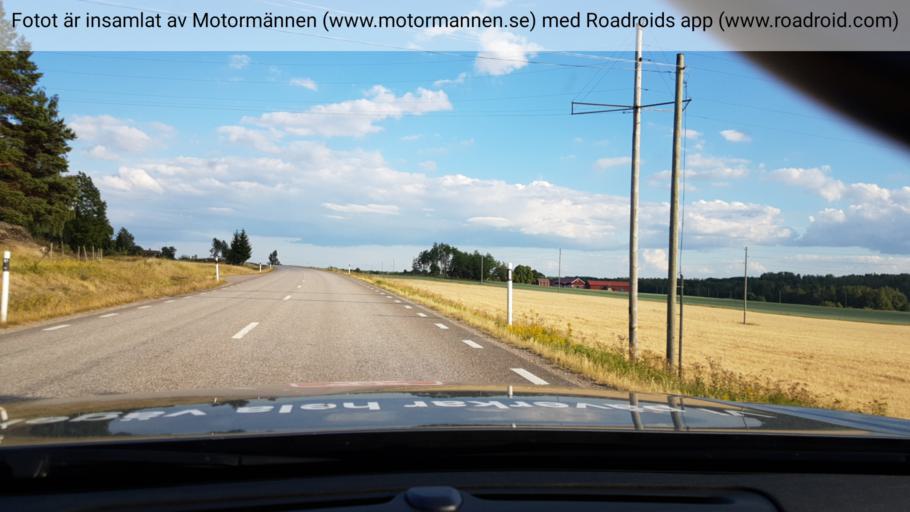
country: SE
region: Uppsala
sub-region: Heby Kommun
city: Morgongava
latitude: 59.8907
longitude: 16.9061
